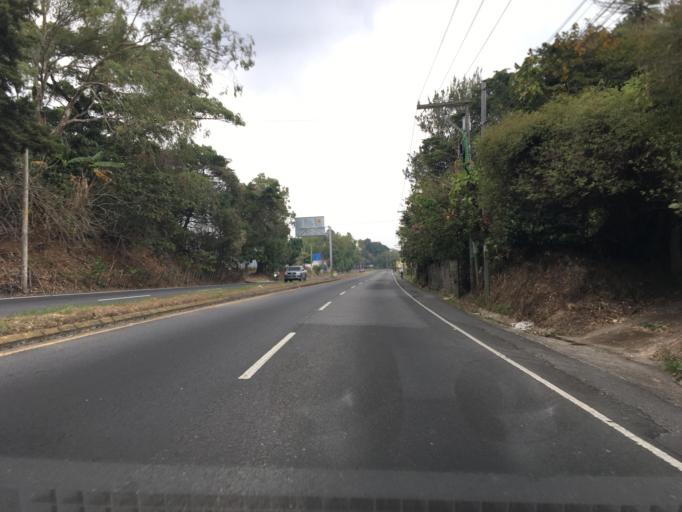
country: GT
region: Guatemala
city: Fraijanes
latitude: 14.4398
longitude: -90.4756
